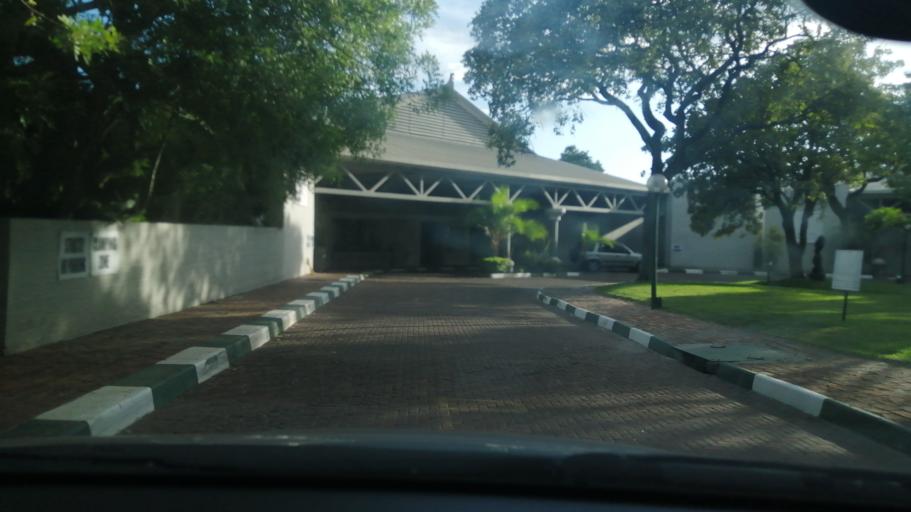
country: ZW
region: Harare
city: Harare
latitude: -17.8328
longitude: 31.1015
